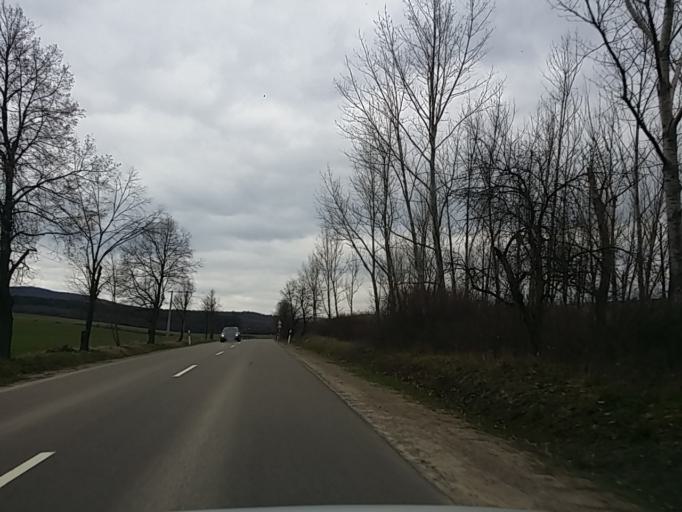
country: HU
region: Heves
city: Verpelet
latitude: 47.8668
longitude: 20.2009
